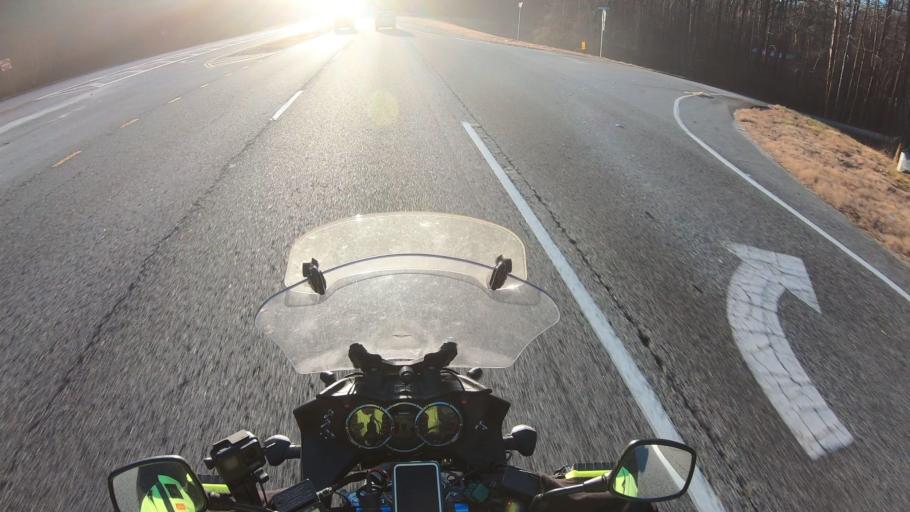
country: US
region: Georgia
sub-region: Lumpkin County
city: Dahlonega
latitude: 34.4518
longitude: -83.9810
